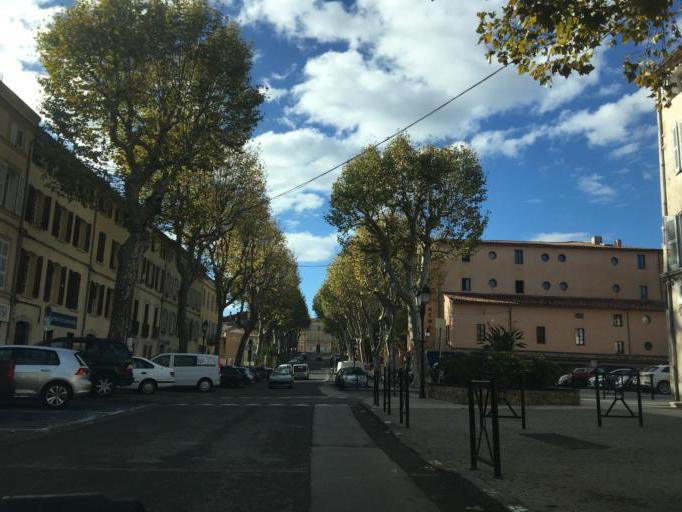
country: FR
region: Provence-Alpes-Cote d'Azur
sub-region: Departement du Var
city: Lorgues
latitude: 43.4931
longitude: 6.3597
